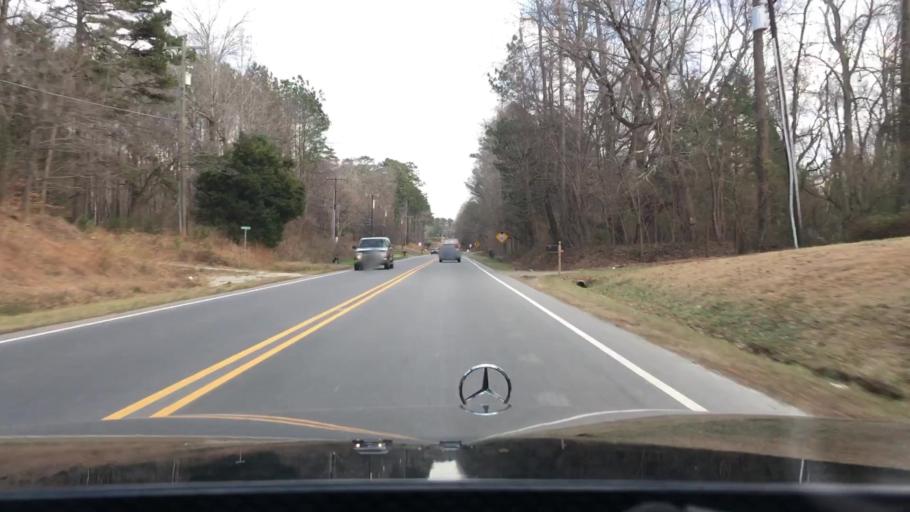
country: US
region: North Carolina
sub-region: Orange County
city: Hillsborough
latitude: 36.0479
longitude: -79.0267
